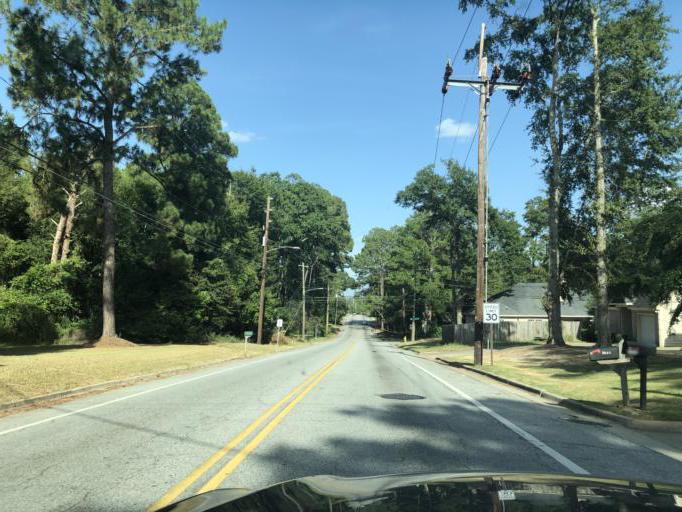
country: US
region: Georgia
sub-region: Muscogee County
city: Columbus
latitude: 32.4842
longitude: -84.9321
